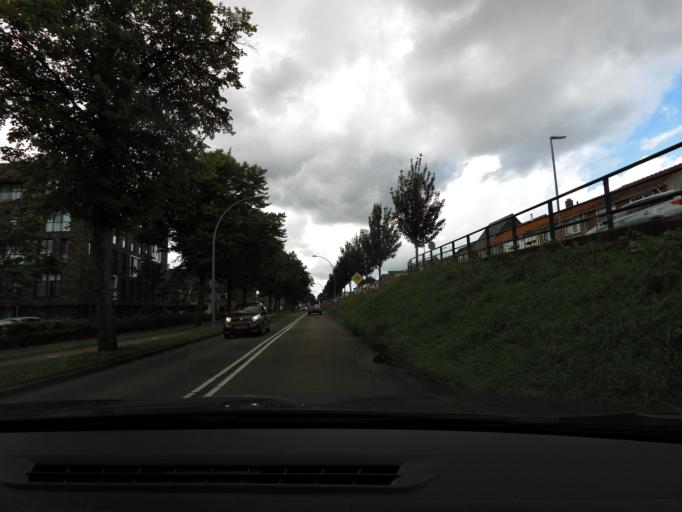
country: NL
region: South Holland
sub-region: Gemeente Oud-Beijerland
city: Oud-Beijerland
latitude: 51.8245
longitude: 4.4223
